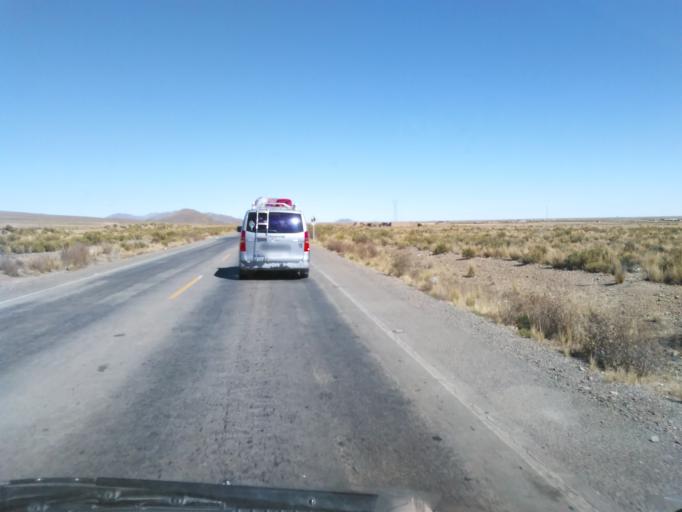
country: BO
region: Oruro
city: Machacamarca
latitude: -18.0668
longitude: -67.0057
